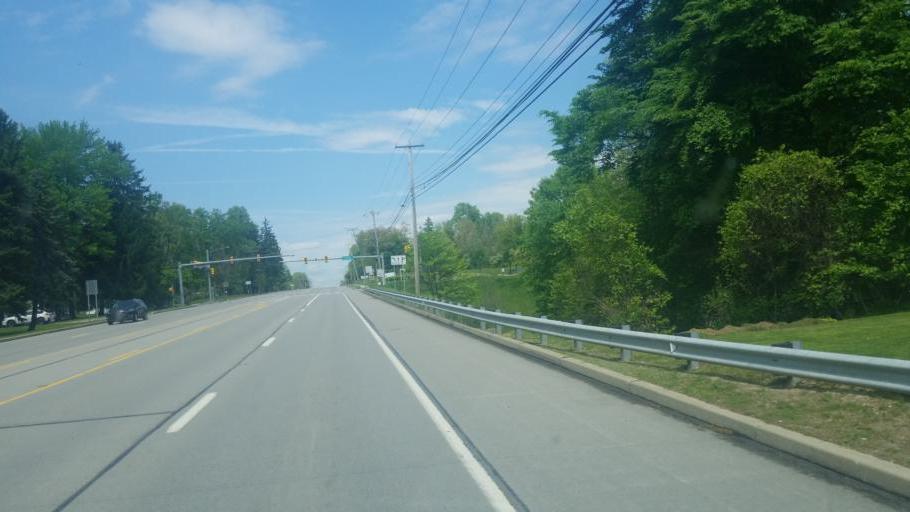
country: US
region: Pennsylvania
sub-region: Mercer County
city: Hermitage
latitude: 41.2167
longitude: -80.4558
